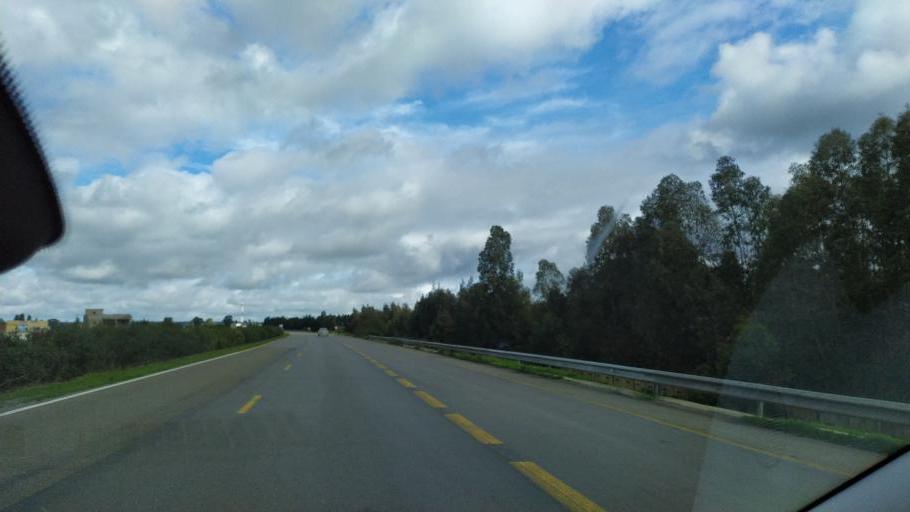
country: MA
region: Gharb-Chrarda-Beni Hssen
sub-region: Kenitra Province
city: Lalla Mimouna
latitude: 34.8789
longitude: -6.2123
